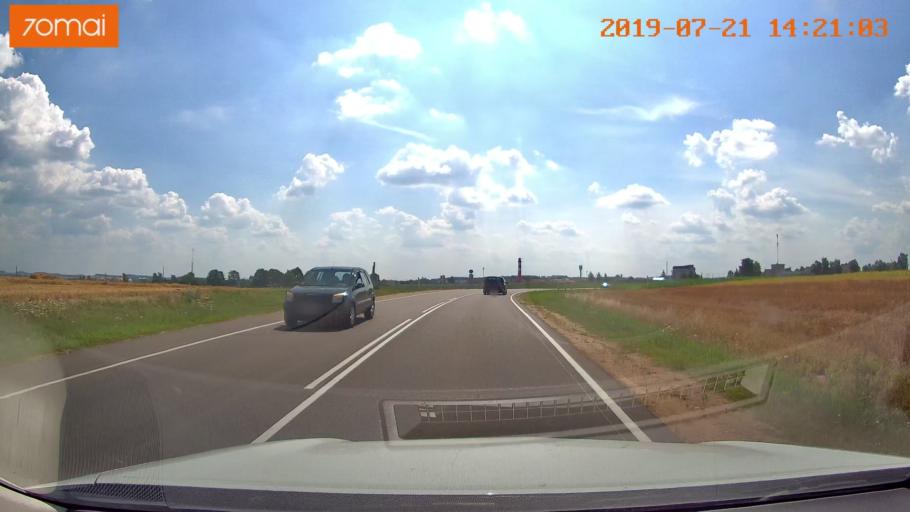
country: BY
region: Grodnenskaya
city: Karelichy
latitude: 53.5793
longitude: 26.1490
